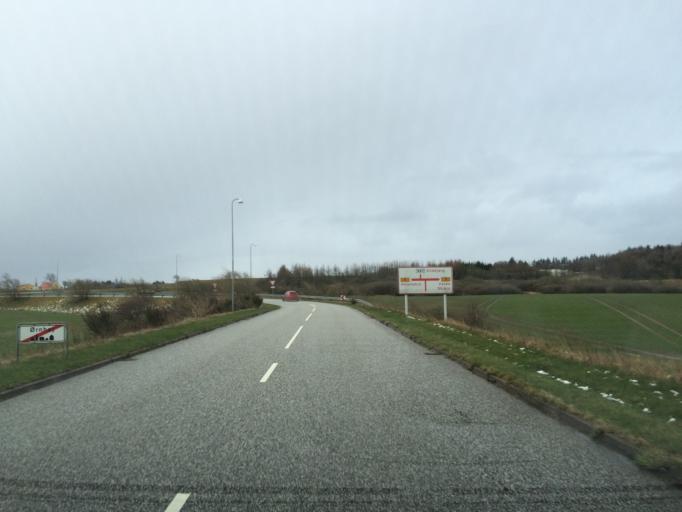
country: DK
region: Central Jutland
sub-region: Ringkobing-Skjern Kommune
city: Videbaek
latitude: 56.1947
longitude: 8.5683
